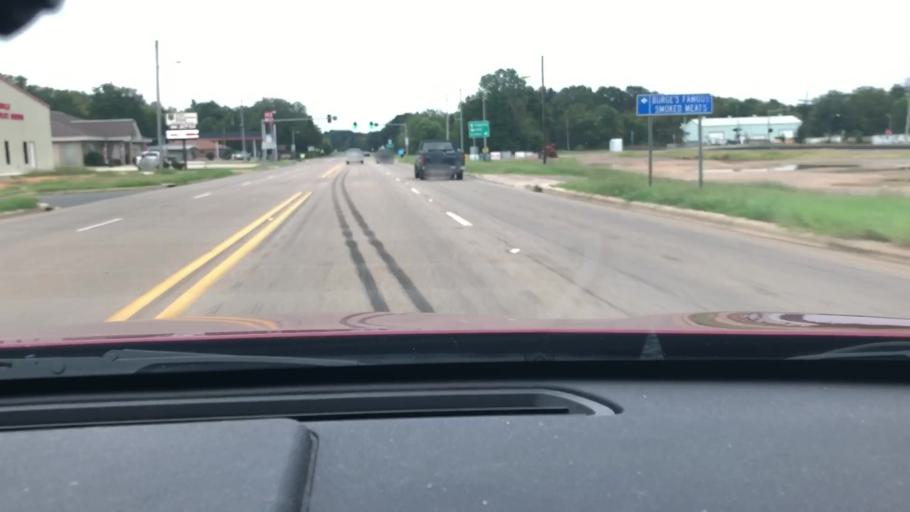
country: US
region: Arkansas
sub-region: Lafayette County
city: Lewisville
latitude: 33.3553
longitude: -93.5781
